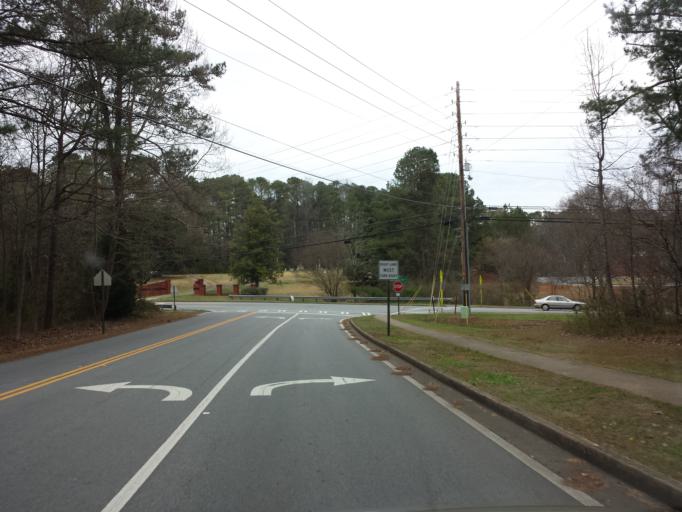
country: US
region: Georgia
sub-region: Cherokee County
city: Woodstock
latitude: 34.0504
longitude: -84.5067
